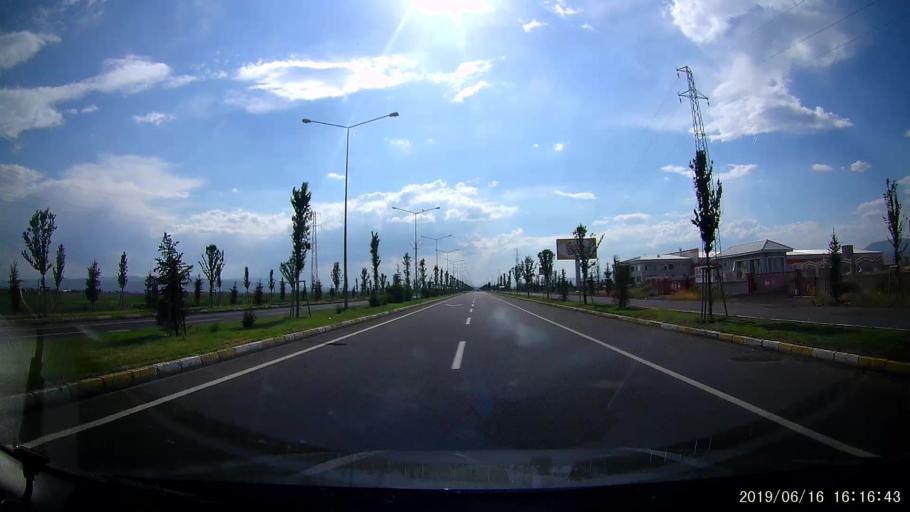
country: TR
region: Erzurum
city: Erzurum
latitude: 39.9631
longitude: 41.2021
